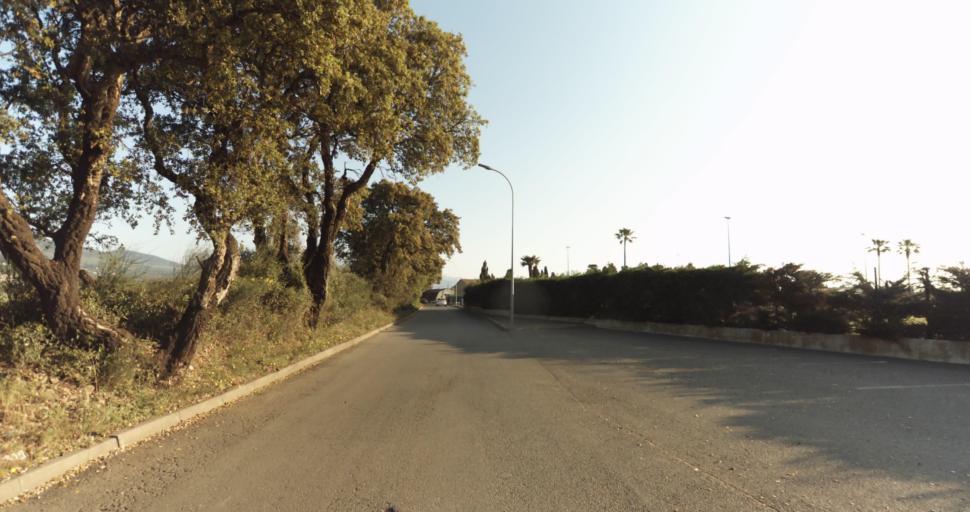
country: FR
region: Corsica
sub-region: Departement de la Haute-Corse
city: Biguglia
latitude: 42.6080
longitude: 9.4439
